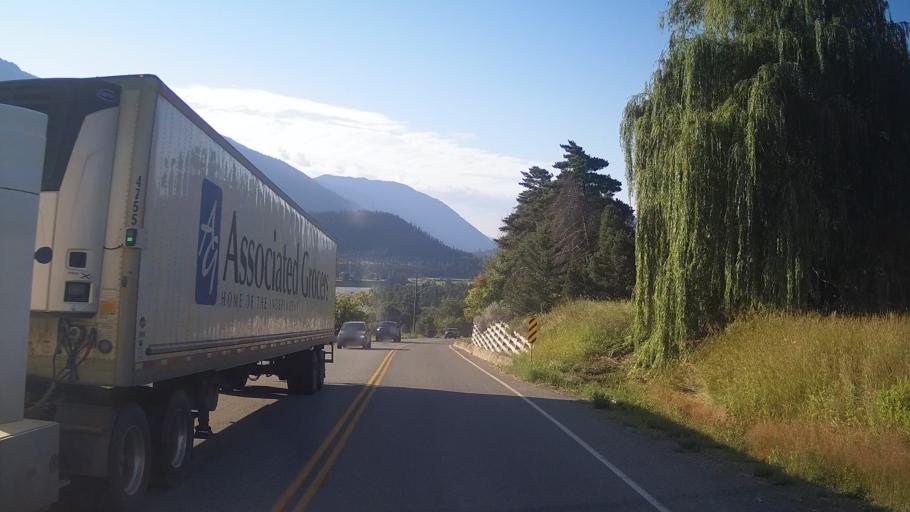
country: CA
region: British Columbia
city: Lillooet
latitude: 50.6852
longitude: -121.9348
